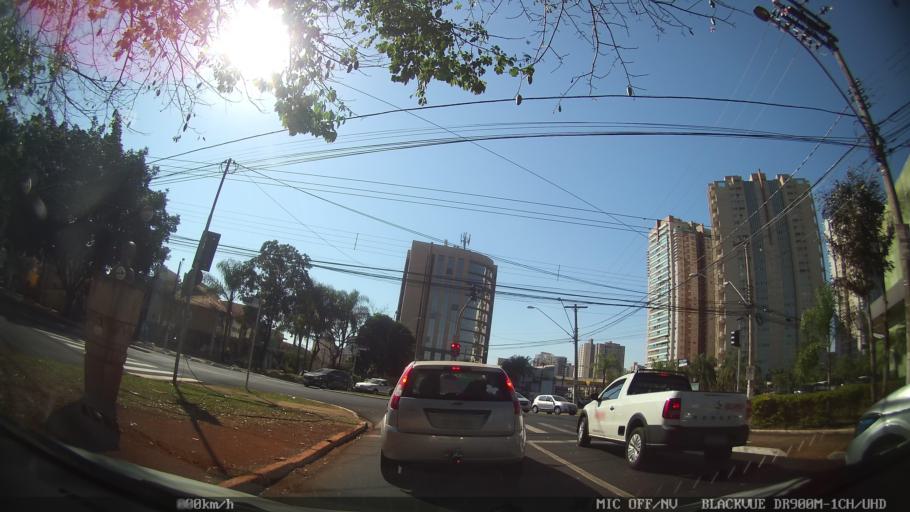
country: BR
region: Sao Paulo
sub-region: Ribeirao Preto
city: Ribeirao Preto
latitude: -21.2116
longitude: -47.8062
